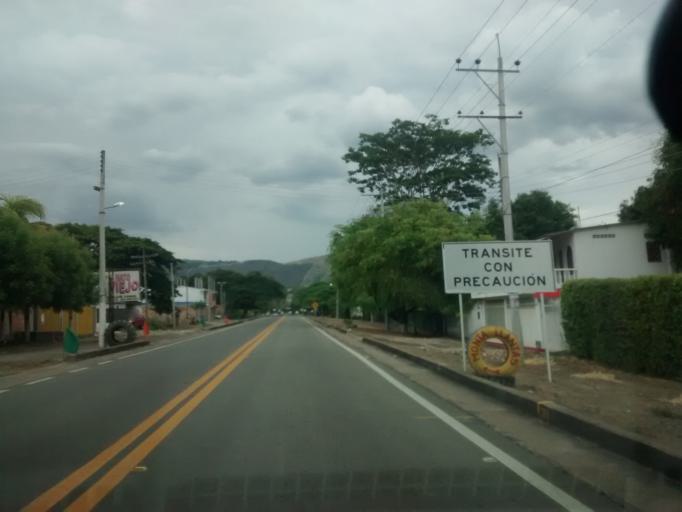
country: CO
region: Cundinamarca
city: Tocaima
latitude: 4.4531
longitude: -74.6478
